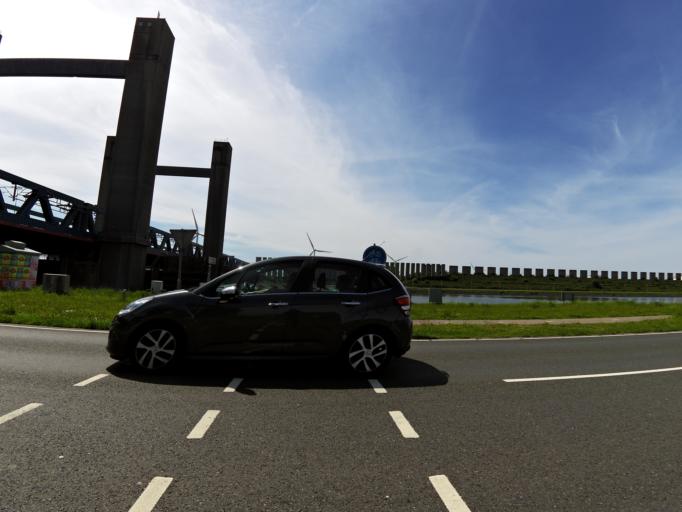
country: NL
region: South Holland
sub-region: Gemeente Maassluis
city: Maassluis
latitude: 51.9020
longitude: 4.2289
